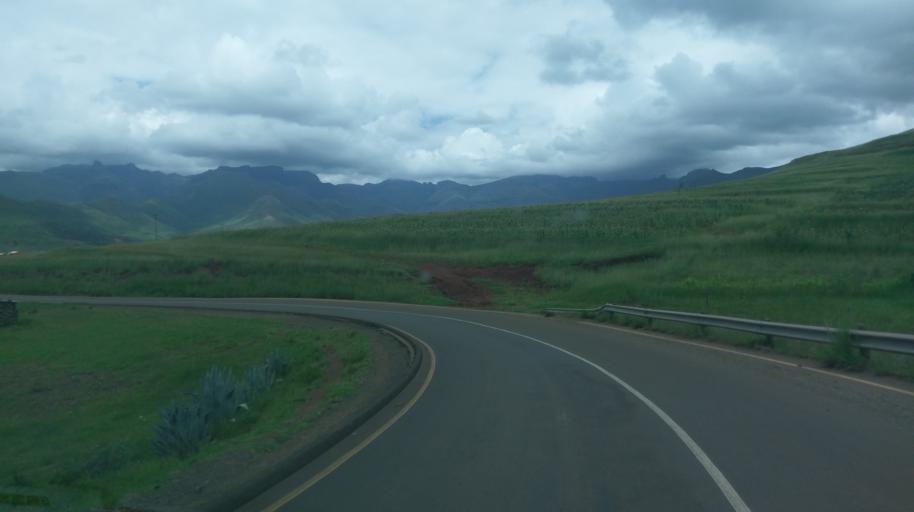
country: LS
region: Leribe
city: Leribe
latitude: -29.0345
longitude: 28.2359
